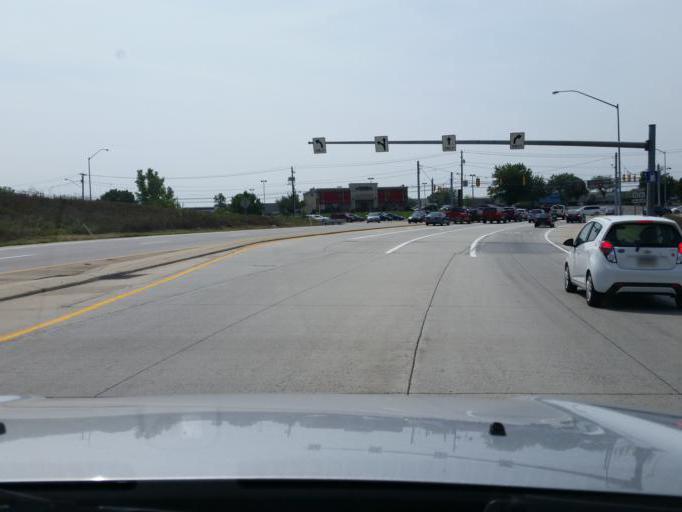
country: US
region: Pennsylvania
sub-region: Cumberland County
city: Shiremanstown
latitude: 40.2399
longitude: -76.9792
